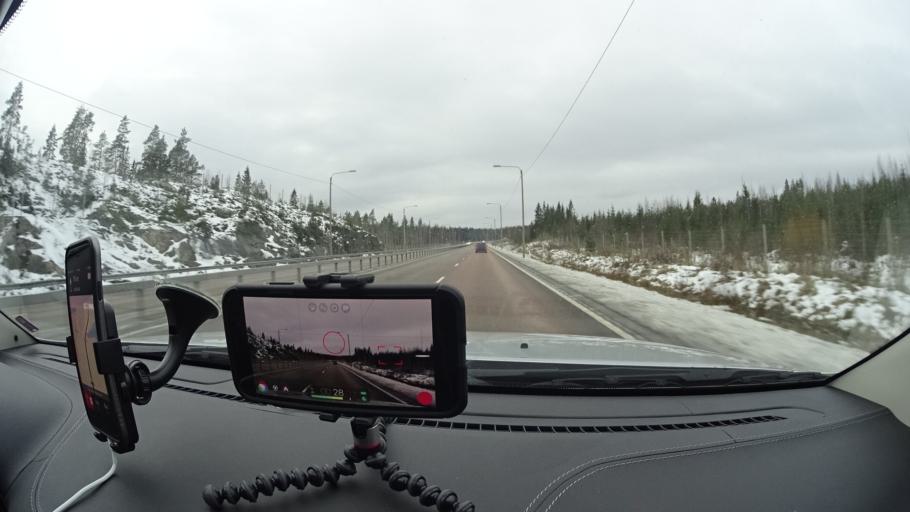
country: FI
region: Paijanne Tavastia
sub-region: Lahti
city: Hartola
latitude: 61.4225
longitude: 26.0230
